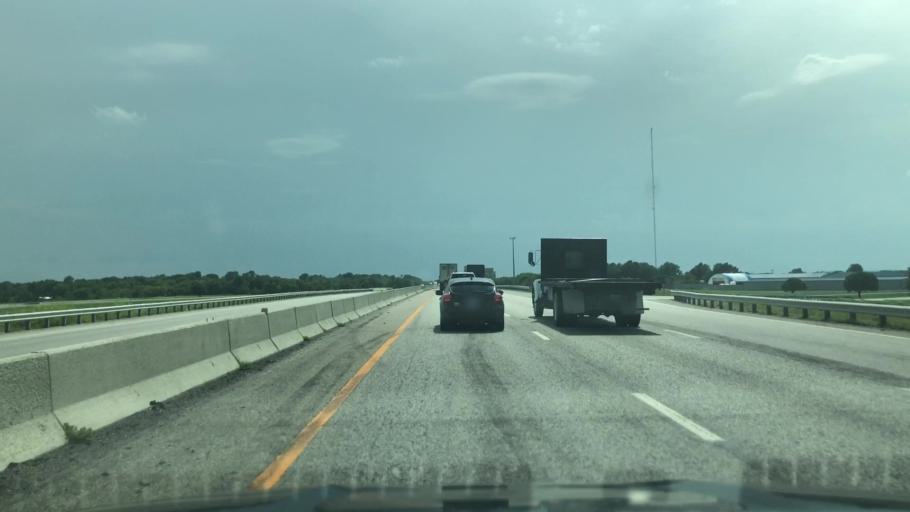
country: US
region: Oklahoma
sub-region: Craig County
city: Vinita
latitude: 36.6343
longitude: -95.1309
